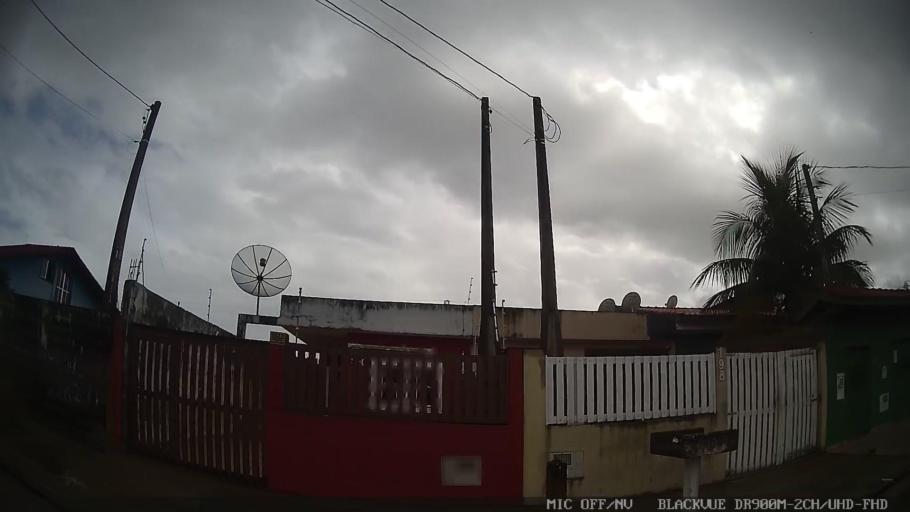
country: BR
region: Sao Paulo
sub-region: Itanhaem
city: Itanhaem
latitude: -24.1907
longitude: -46.8268
